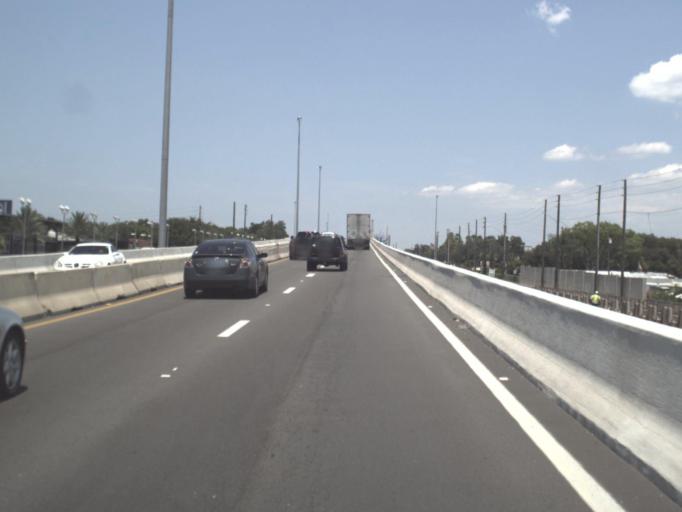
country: US
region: Florida
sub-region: Pinellas County
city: South Highpoint
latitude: 27.9511
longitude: -82.7301
